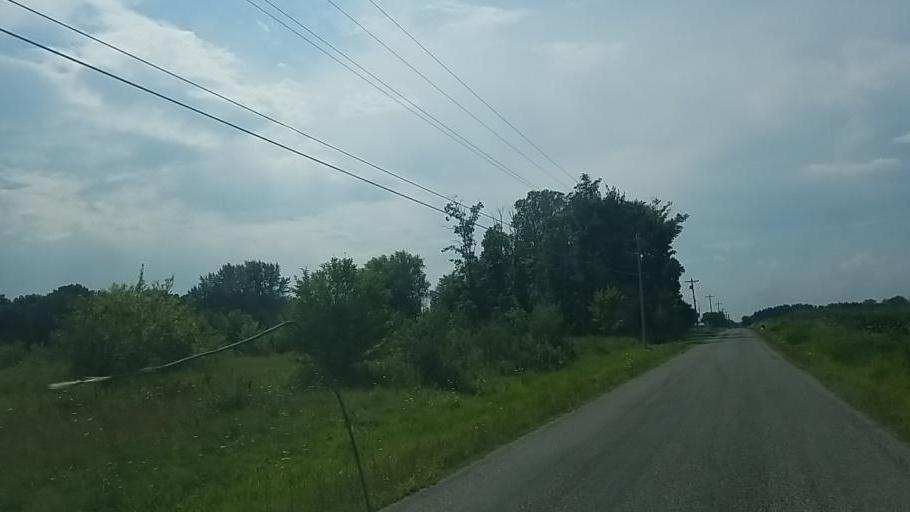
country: US
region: Ohio
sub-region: Medina County
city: Lodi
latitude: 41.0906
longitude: -81.9955
